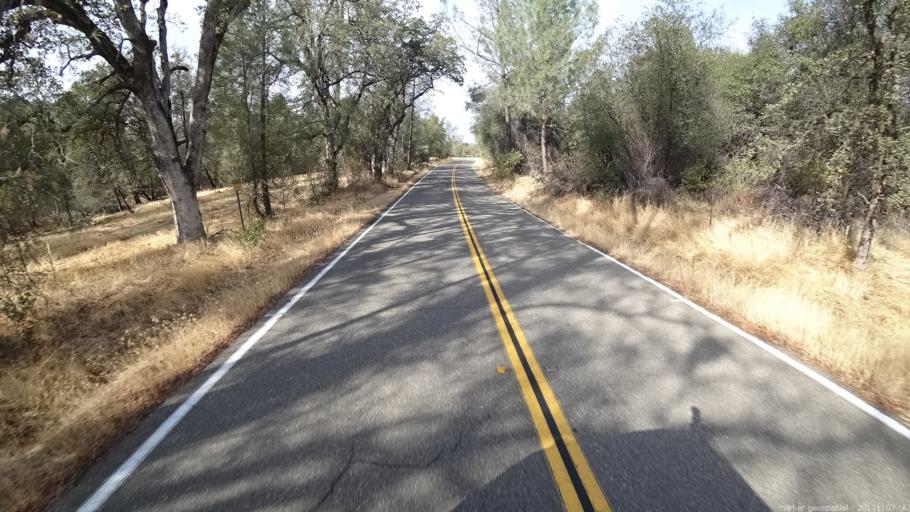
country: US
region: California
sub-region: Shasta County
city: Shasta
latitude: 40.5020
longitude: -122.5282
